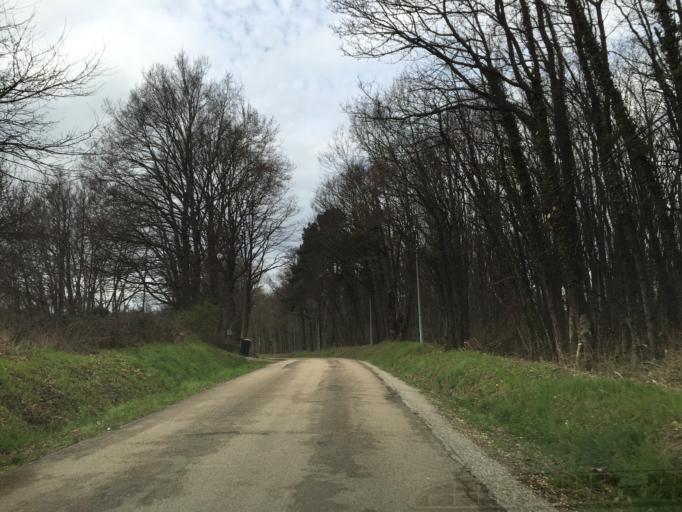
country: FR
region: Bourgogne
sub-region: Departement de l'Yonne
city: Charbuy
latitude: 47.8330
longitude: 3.4585
